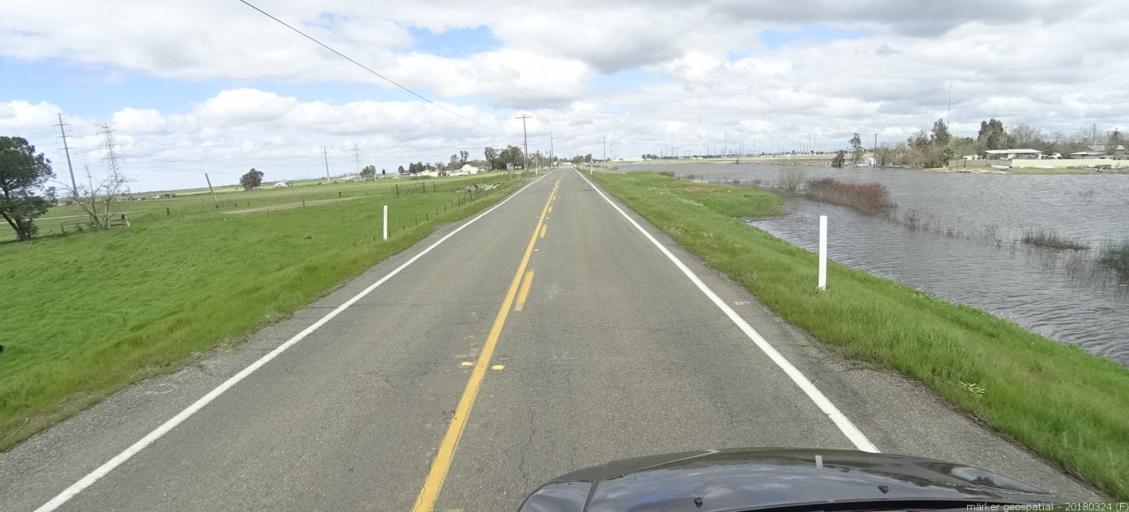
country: US
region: California
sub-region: Sacramento County
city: Elverta
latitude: 38.6980
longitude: -121.4856
